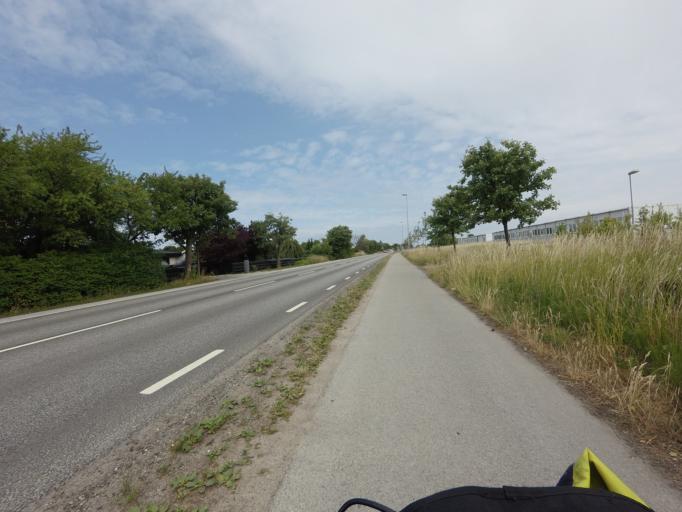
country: SE
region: Skane
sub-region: Malmo
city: Bunkeflostrand
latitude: 55.5393
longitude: 12.9199
